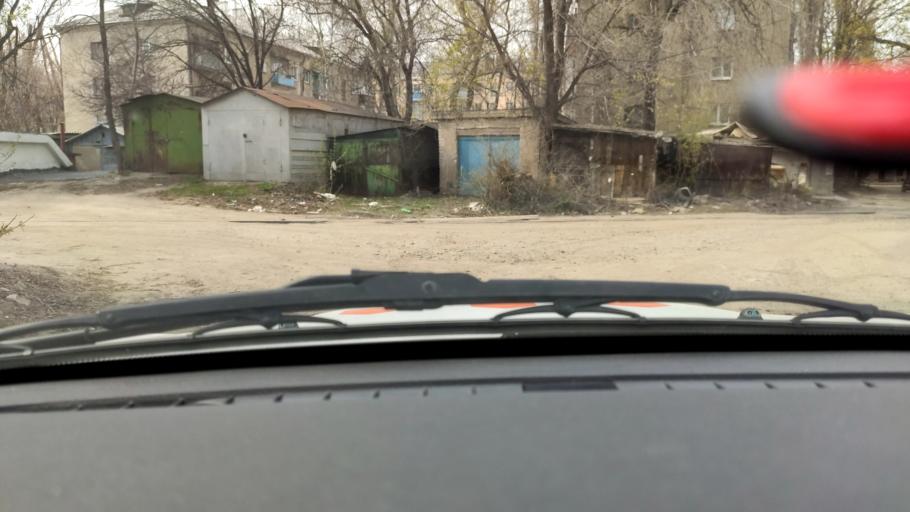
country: RU
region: Voronezj
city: Voronezh
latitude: 51.6720
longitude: 39.1723
